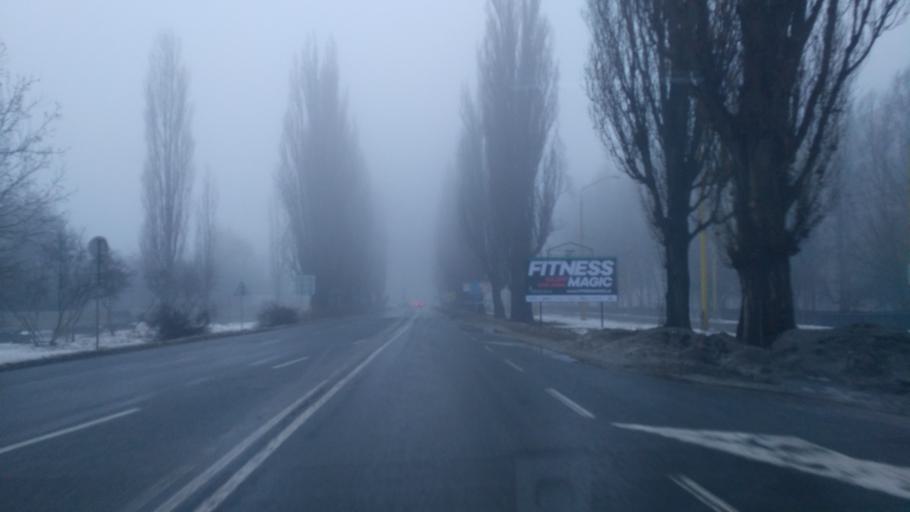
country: SK
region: Kosicky
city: Kosice
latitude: 48.6801
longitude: 21.2937
